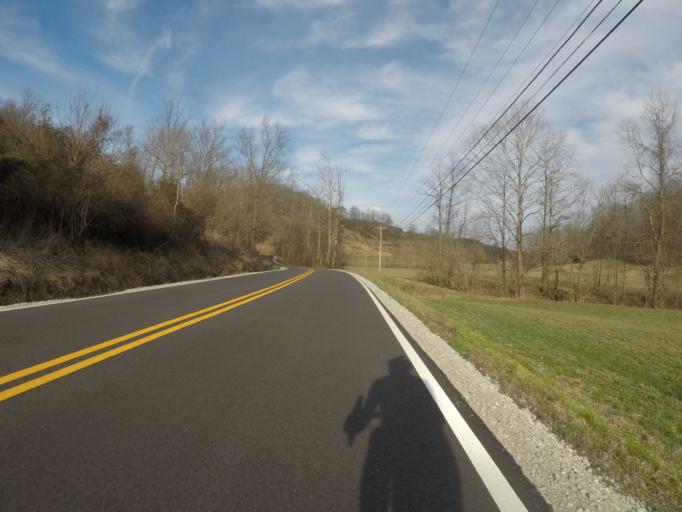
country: US
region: West Virginia
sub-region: Cabell County
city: Huntington
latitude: 38.4802
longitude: -82.4952
